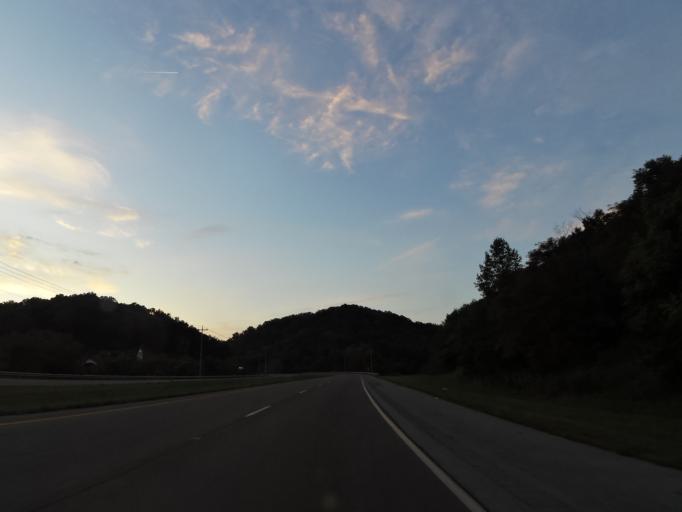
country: US
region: Tennessee
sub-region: Carter County
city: Elizabethton
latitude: 36.3643
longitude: -82.2071
